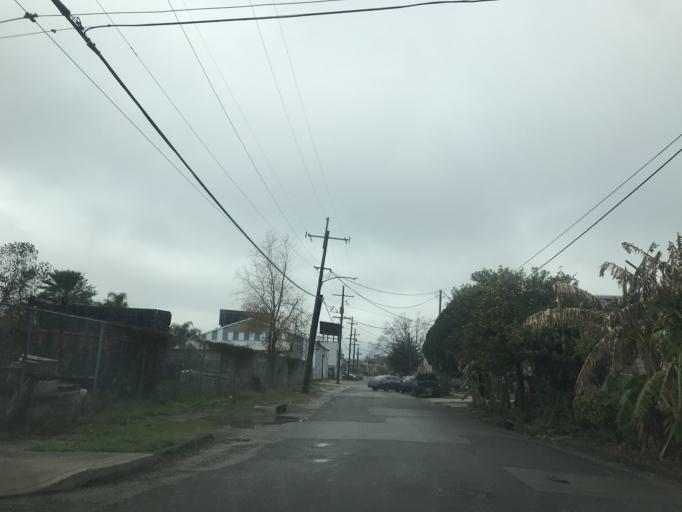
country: US
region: Louisiana
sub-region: Orleans Parish
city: New Orleans
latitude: 29.9732
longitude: -90.1089
